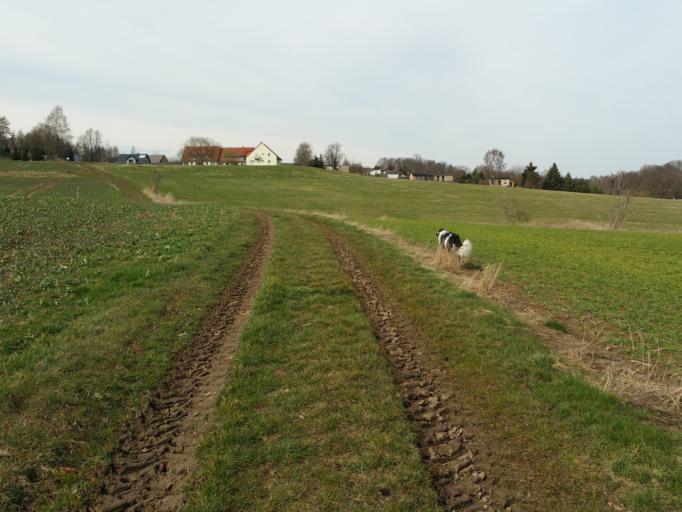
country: DE
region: Saxony
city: Niederschona
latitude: 50.9504
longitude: 13.3993
